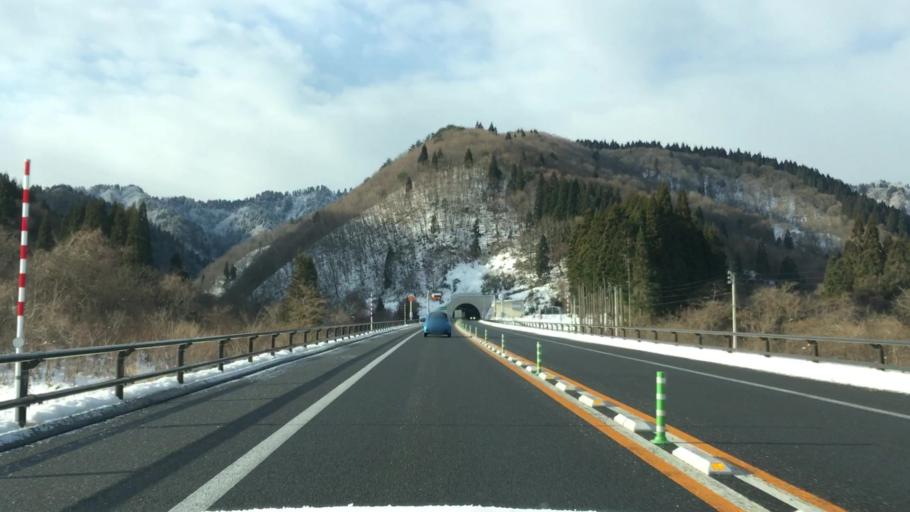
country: JP
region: Akita
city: Odate
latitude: 40.2316
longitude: 140.4917
